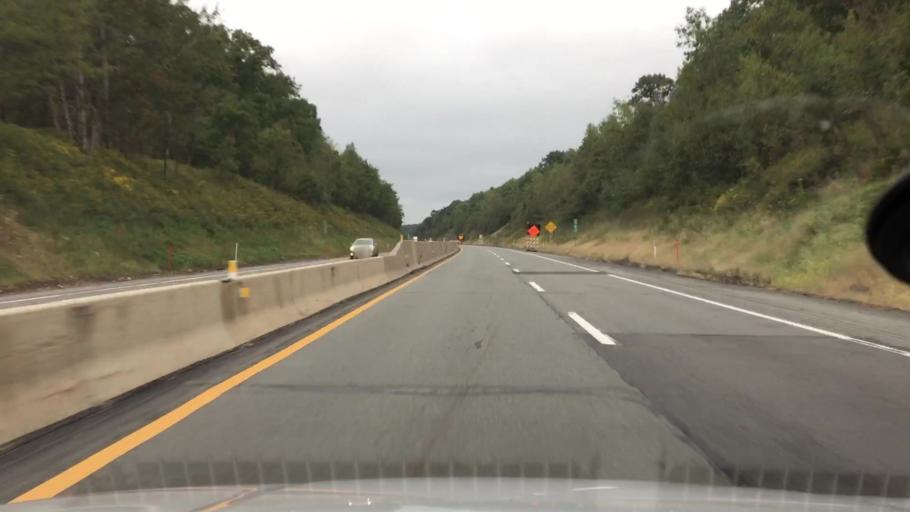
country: US
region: Pennsylvania
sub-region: Luzerne County
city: White Haven
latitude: 41.1055
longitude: -75.7506
